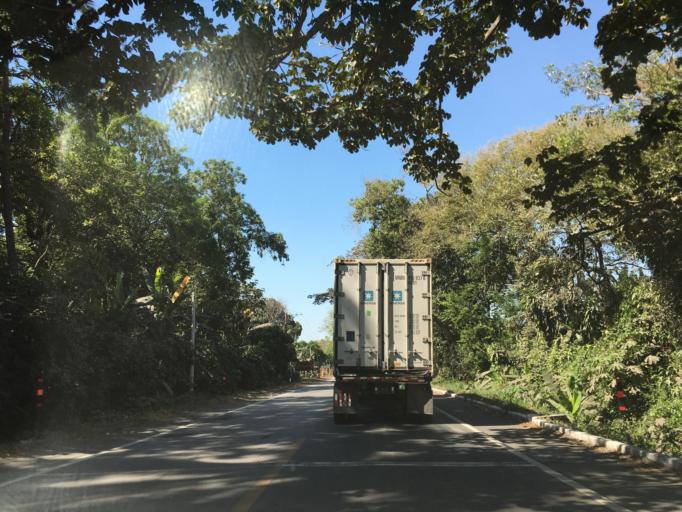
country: GT
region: Escuintla
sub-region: Municipio de Masagua
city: Masagua
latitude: 14.1831
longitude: -90.8638
